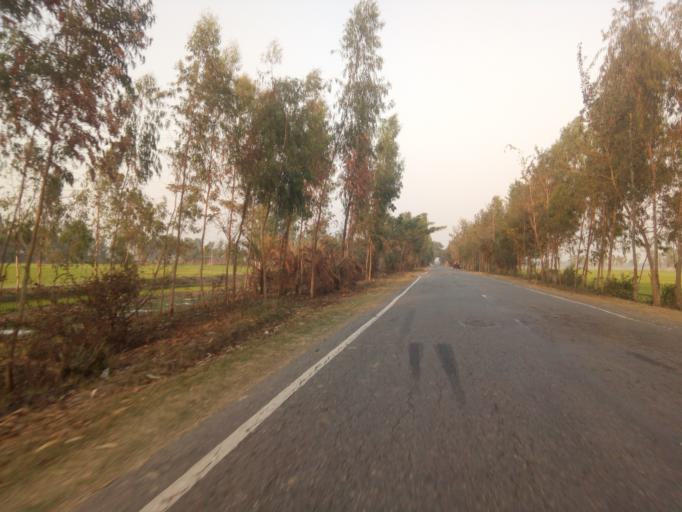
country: BD
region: Rajshahi
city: Bogra
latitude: 24.5756
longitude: 89.2196
